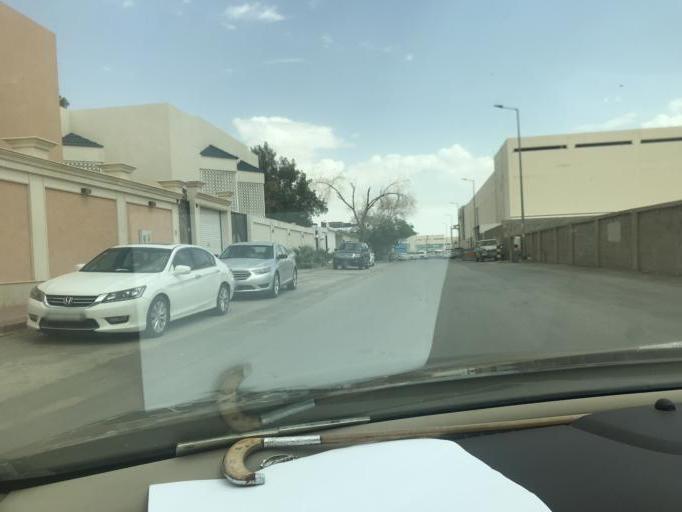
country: SA
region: Ar Riyad
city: Riyadh
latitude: 24.7295
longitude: 46.7814
